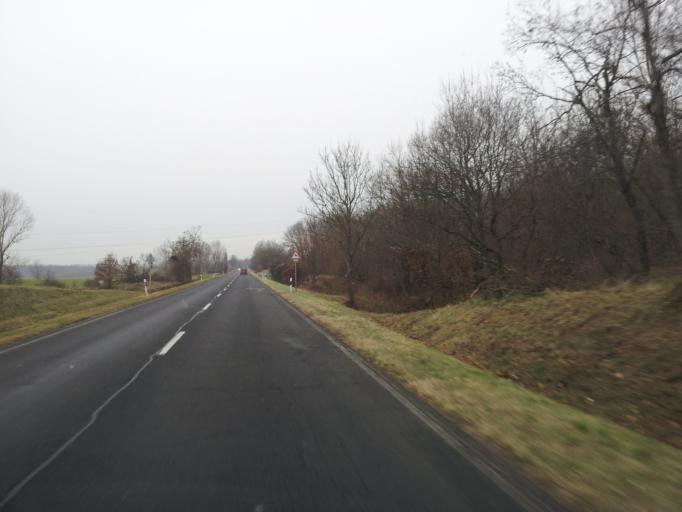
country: HU
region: Veszprem
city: Ajka
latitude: 47.1300
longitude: 17.5047
